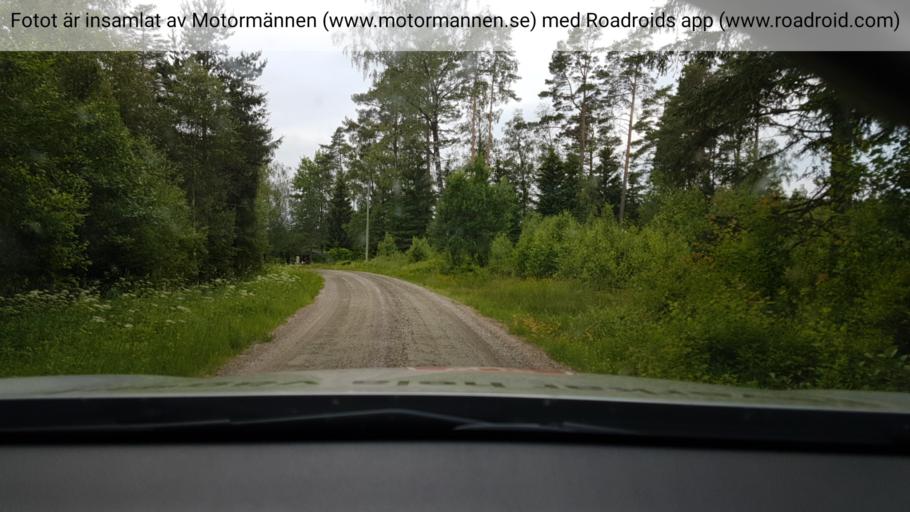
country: SE
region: Joenkoeping
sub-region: Mullsjo Kommun
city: Mullsjoe
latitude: 57.9191
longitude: 13.7095
